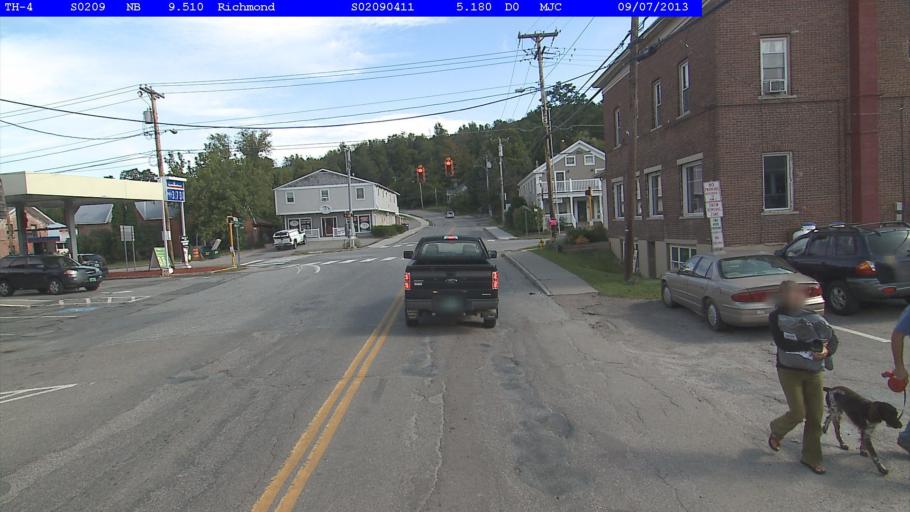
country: US
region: Vermont
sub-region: Chittenden County
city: Williston
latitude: 44.4049
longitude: -72.9932
